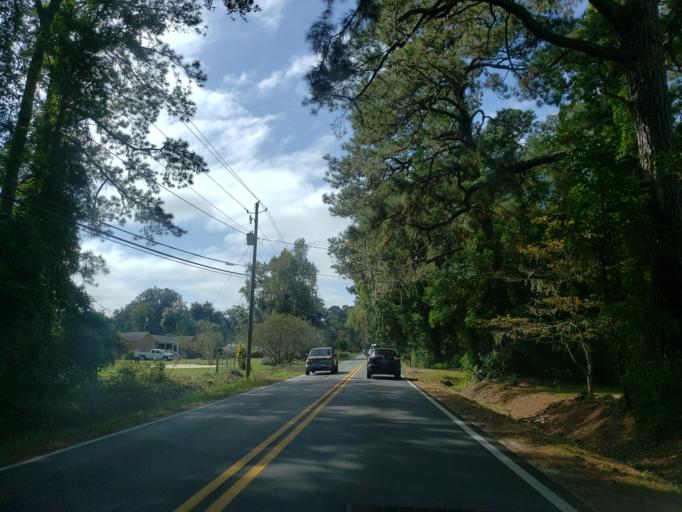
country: US
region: Georgia
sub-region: Chatham County
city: Montgomery
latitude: 31.9479
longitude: -81.1075
